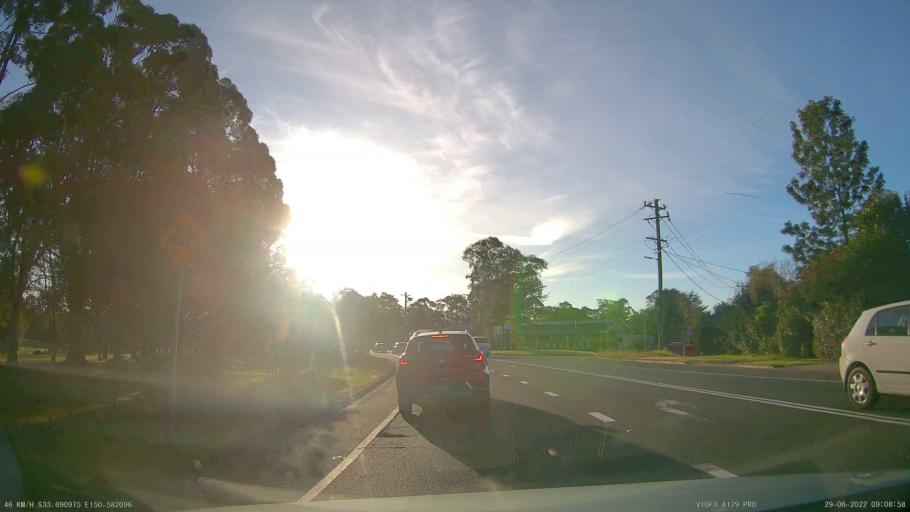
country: AU
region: New South Wales
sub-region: Blue Mountains Municipality
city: Blaxland
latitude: -33.6909
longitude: 150.5824
